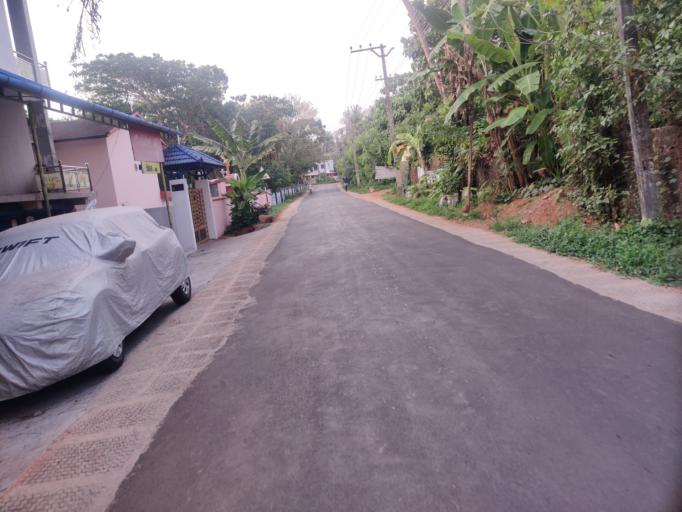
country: IN
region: Kerala
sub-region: Kozhikode
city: Mavoor
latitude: 11.2613
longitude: 75.9504
